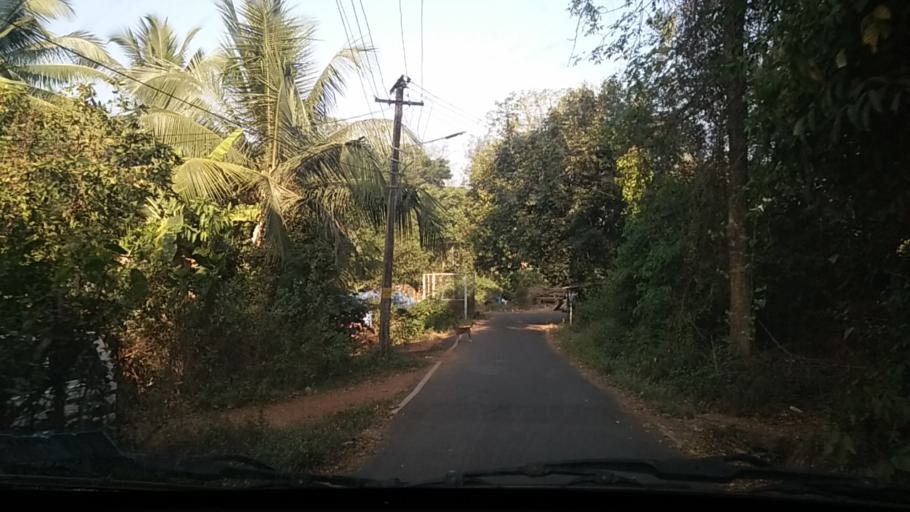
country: IN
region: Goa
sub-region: South Goa
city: Curchorem
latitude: 15.2640
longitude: 74.1134
